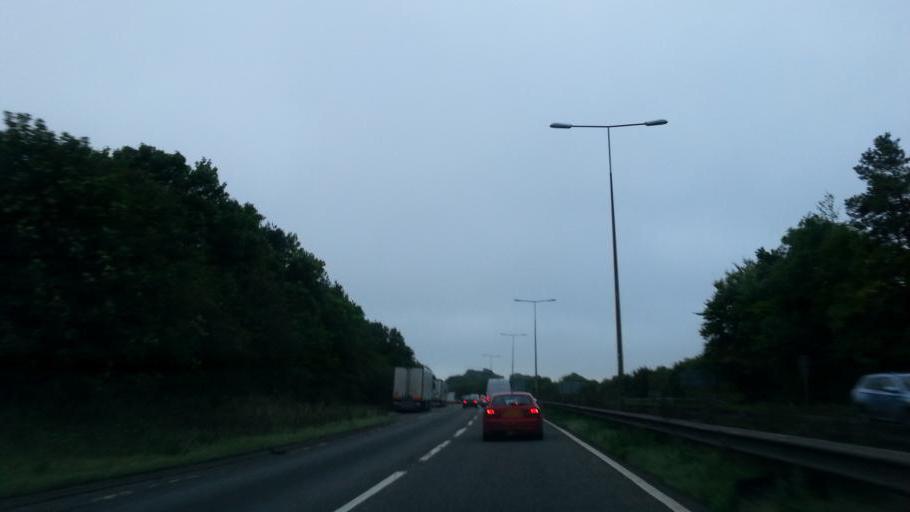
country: GB
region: England
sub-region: District of Rutland
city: Greetham
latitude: 52.8138
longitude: -0.6203
